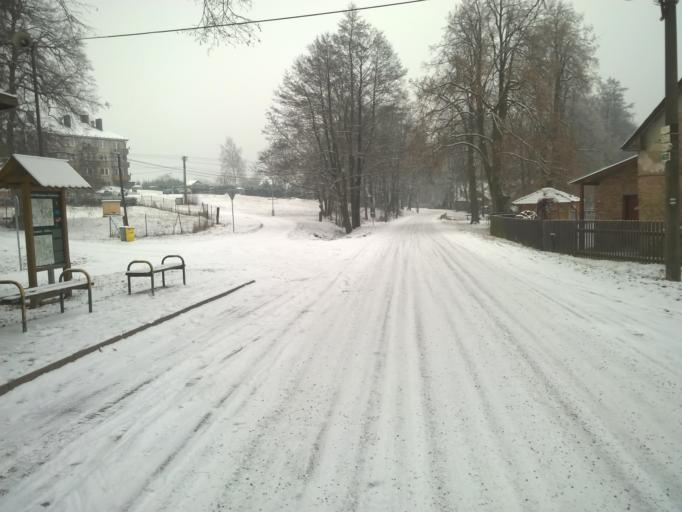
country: CZ
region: Olomoucky
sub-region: Okres Olomouc
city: Sternberk
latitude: 49.7373
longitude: 17.3476
